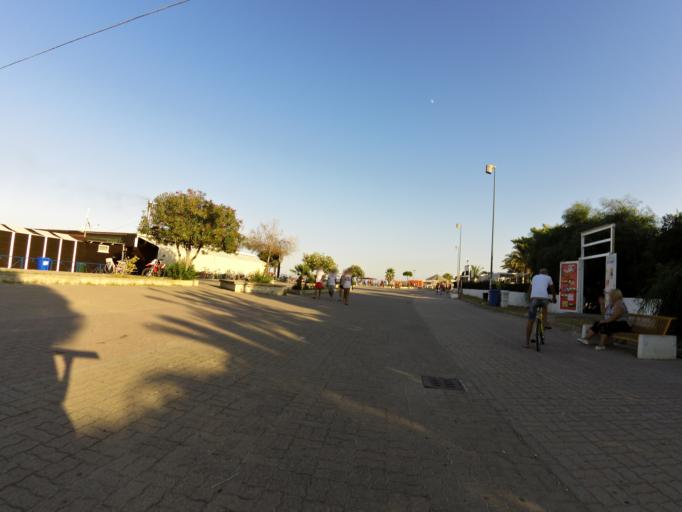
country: IT
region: Calabria
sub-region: Provincia di Catanzaro
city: Soverato Marina
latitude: 38.6890
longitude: 16.5547
